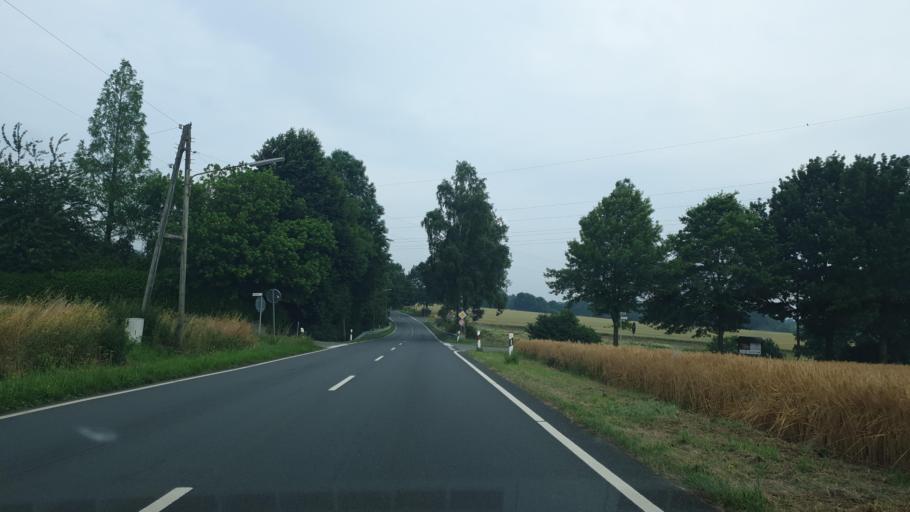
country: DE
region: North Rhine-Westphalia
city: Bad Oeynhausen
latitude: 52.2492
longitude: 8.7980
